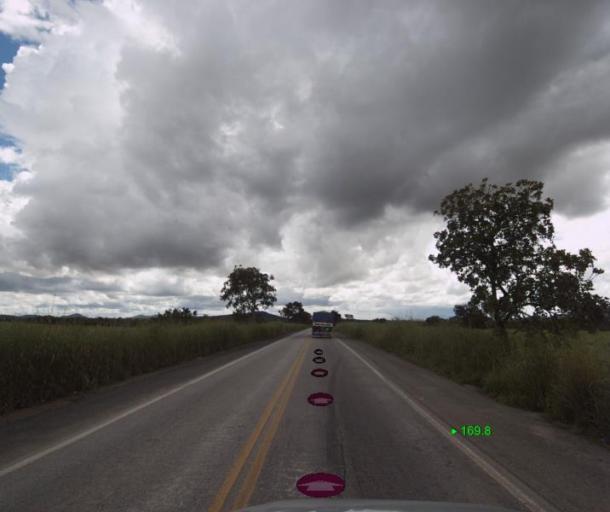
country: BR
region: Goias
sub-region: Uruacu
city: Uruacu
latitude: -14.2594
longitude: -49.1421
